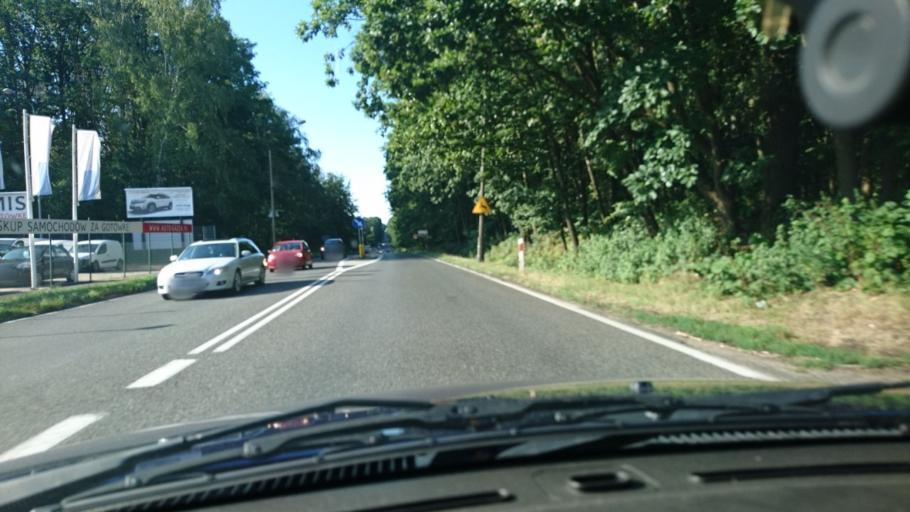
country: PL
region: Silesian Voivodeship
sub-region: Gliwice
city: Gliwice
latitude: 50.3253
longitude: 18.6612
